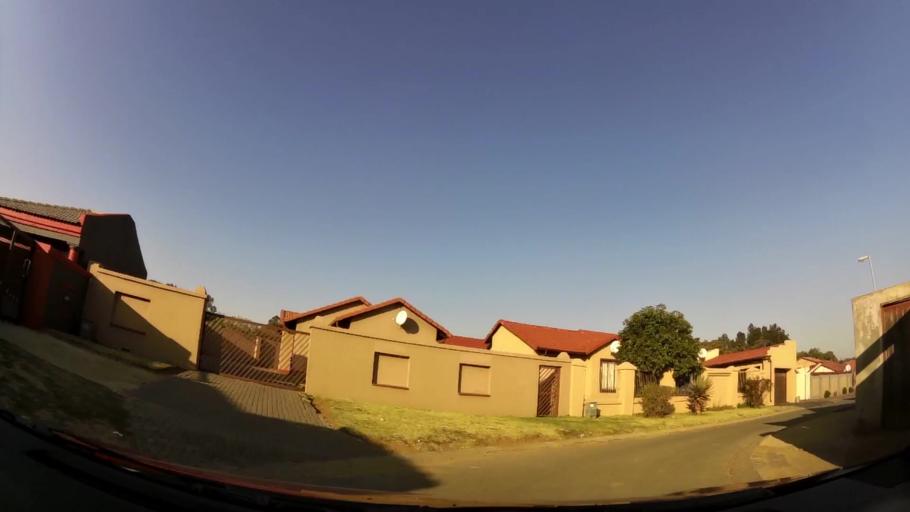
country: ZA
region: Gauteng
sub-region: City of Johannesburg Metropolitan Municipality
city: Soweto
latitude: -26.2794
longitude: 27.9666
